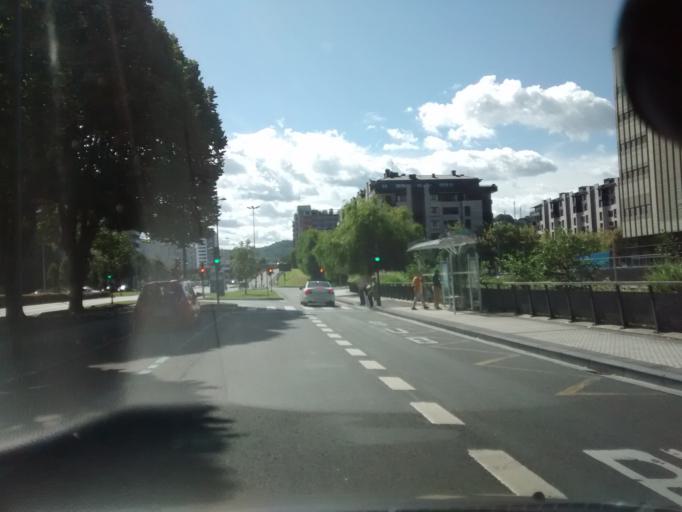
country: ES
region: Basque Country
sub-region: Provincia de Guipuzcoa
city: San Sebastian
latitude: 43.3052
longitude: -2.0070
